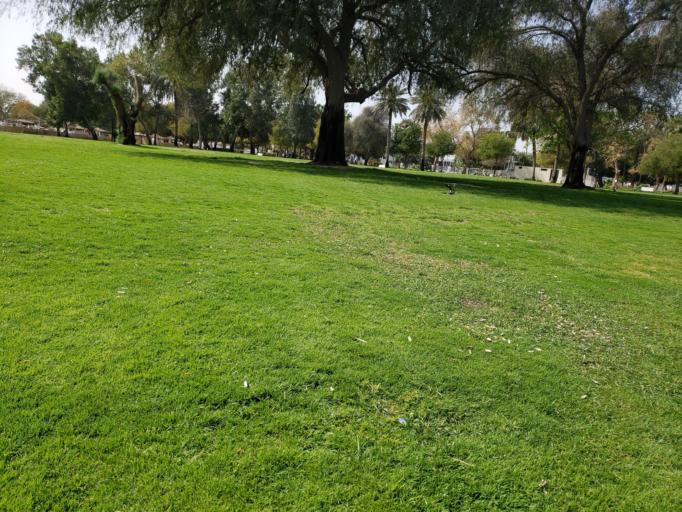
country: AE
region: Dubai
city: Dubai
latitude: 25.1871
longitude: 55.2434
